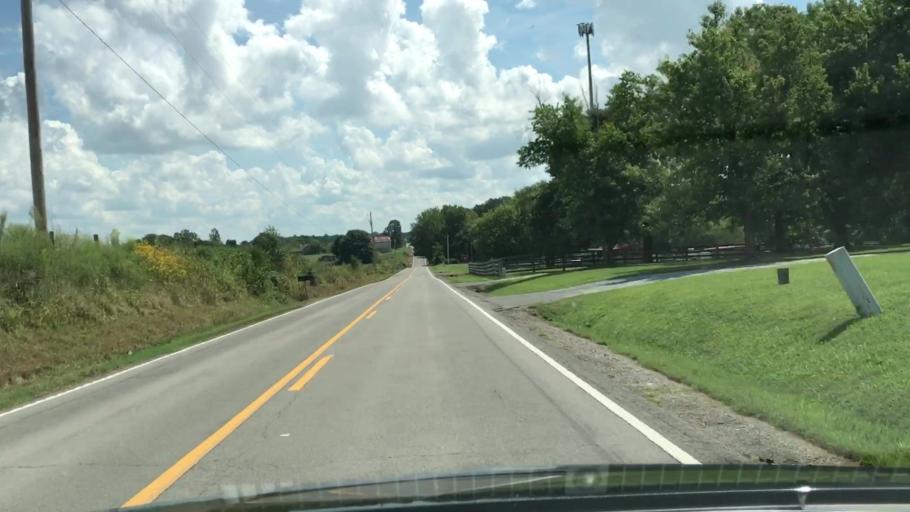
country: US
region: Tennessee
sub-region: Robertson County
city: Springfield
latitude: 36.5989
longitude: -86.9135
